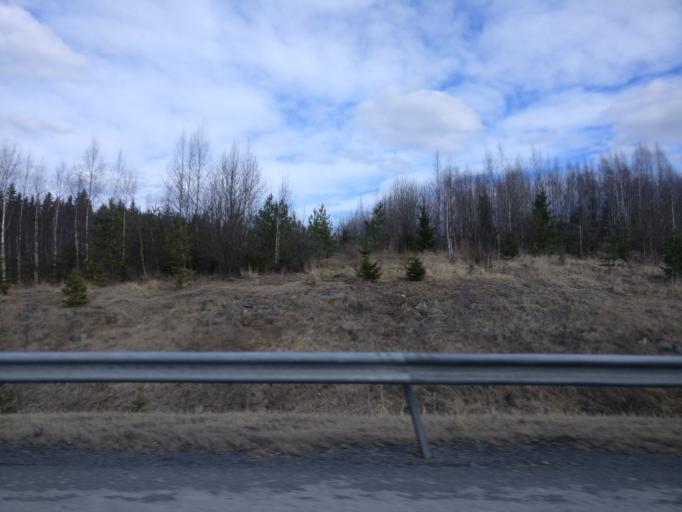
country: FI
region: Pirkanmaa
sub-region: Tampere
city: Lempaeaelae
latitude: 61.3341
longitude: 23.7962
